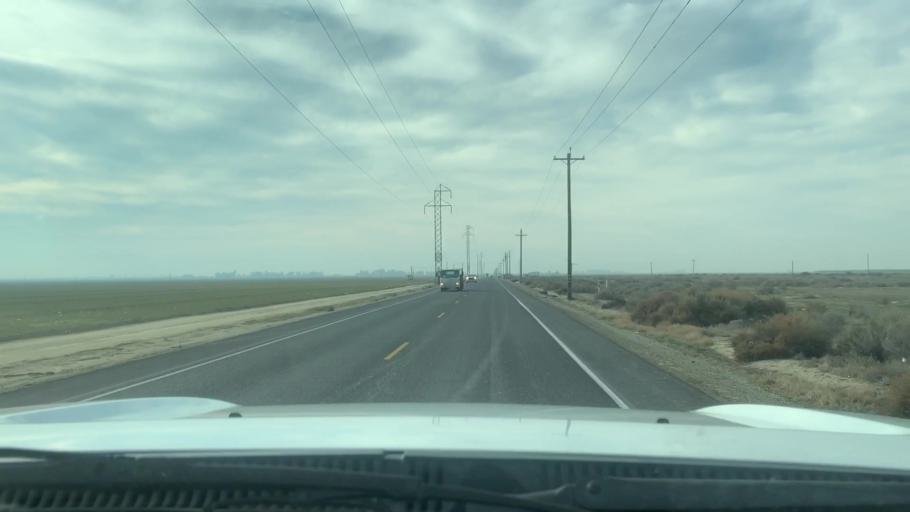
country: US
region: California
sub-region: Kern County
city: Shafter
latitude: 35.4421
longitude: -119.3633
